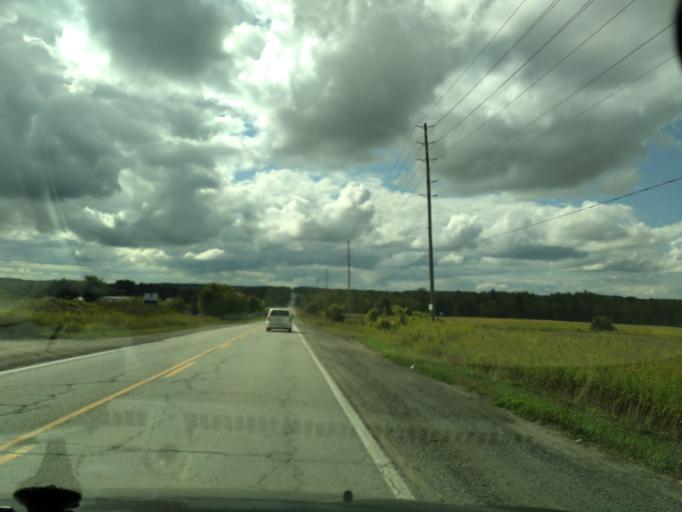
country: CA
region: Ontario
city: Innisfil
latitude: 44.2979
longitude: -79.6230
